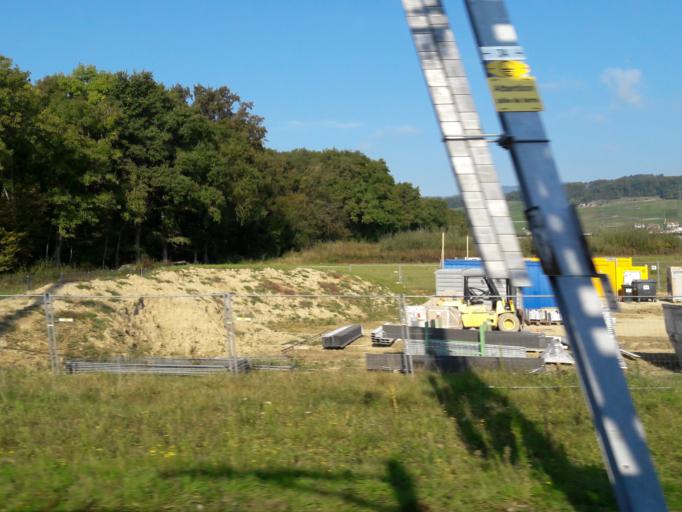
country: CH
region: Vaud
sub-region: Nyon District
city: Gland
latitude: 46.4311
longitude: 6.2807
